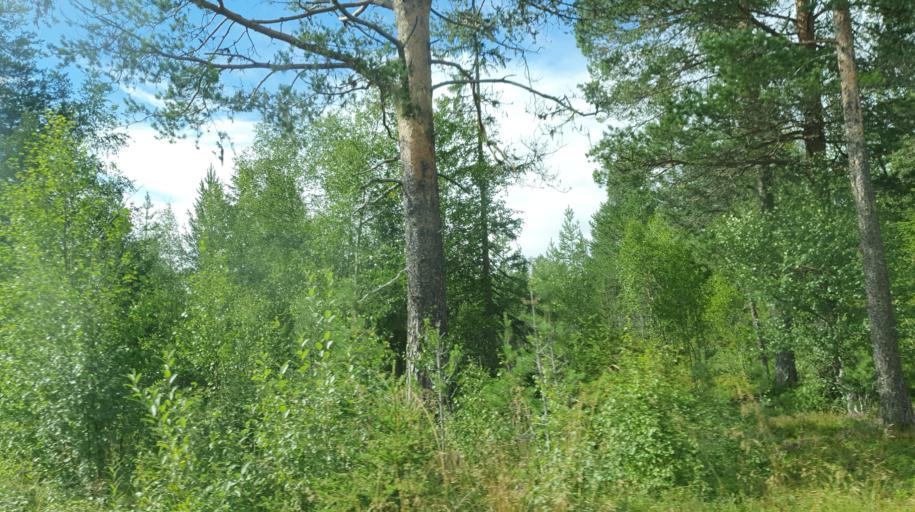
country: NO
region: Nord-Trondelag
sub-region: Levanger
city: Skogn
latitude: 63.5806
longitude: 11.2462
